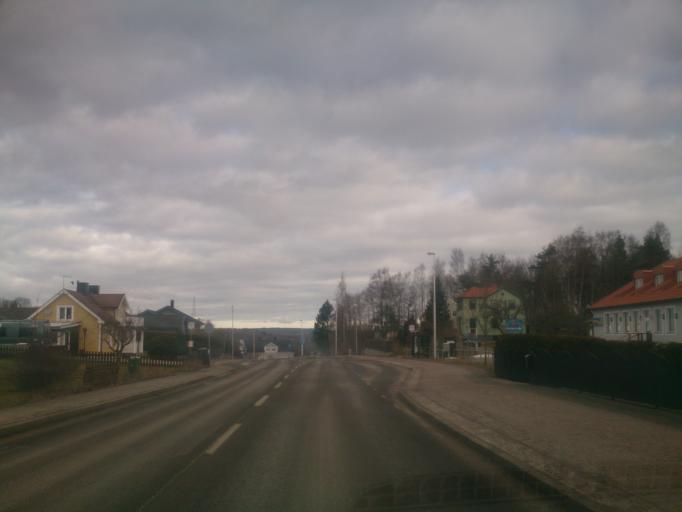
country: SE
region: OEstergoetland
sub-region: Motala Kommun
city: Motala
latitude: 58.5279
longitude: 15.0548
